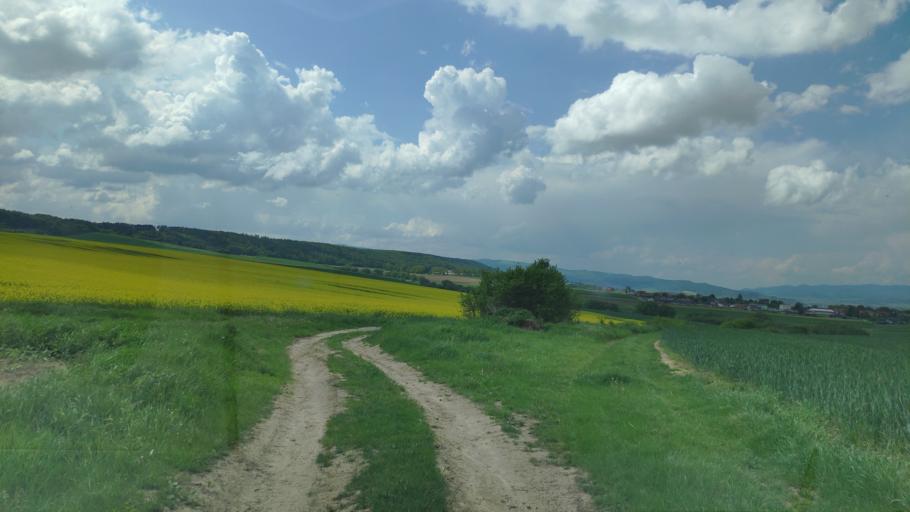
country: SK
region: Presovsky
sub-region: Okres Presov
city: Presov
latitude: 49.0307
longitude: 21.1671
